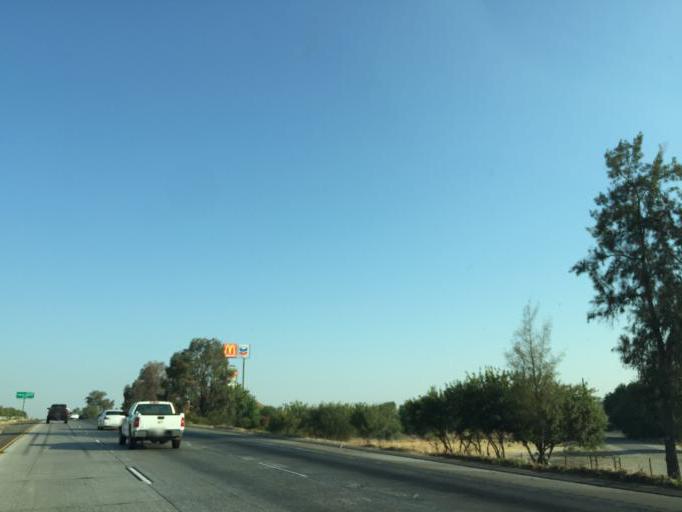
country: US
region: California
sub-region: Fresno County
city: Fowler
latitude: 36.6249
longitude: -119.6825
